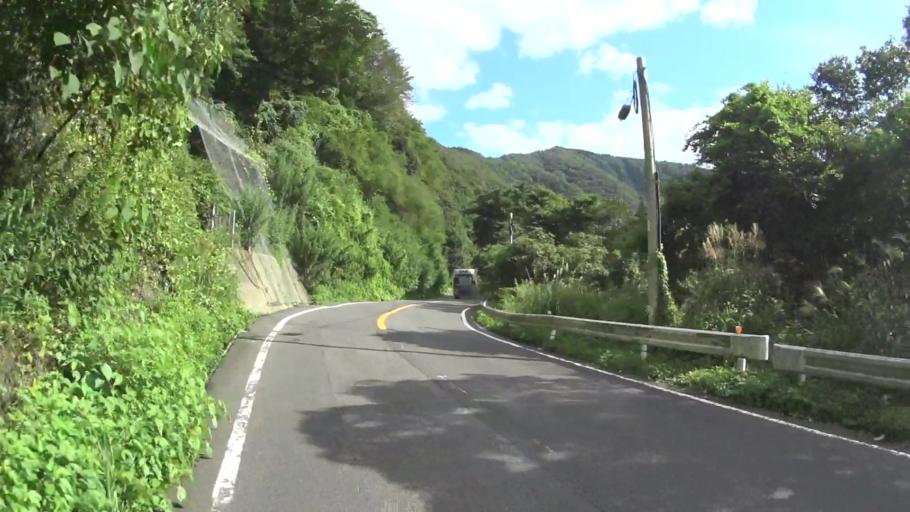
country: JP
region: Kyoto
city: Uji
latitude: 34.8995
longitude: 135.8683
